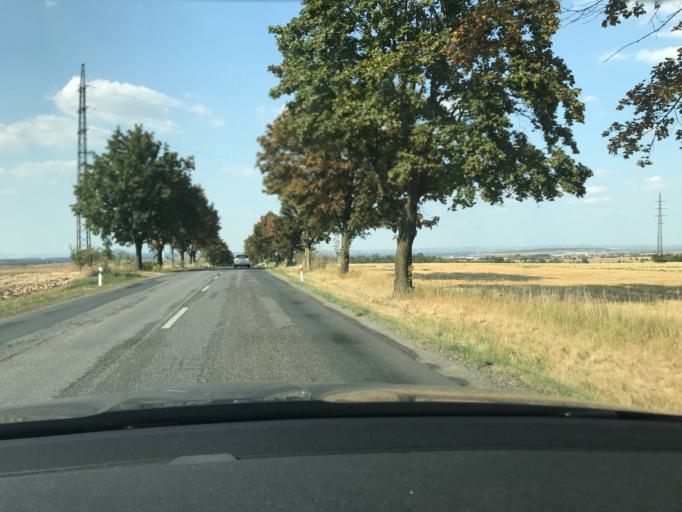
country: CZ
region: Central Bohemia
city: Kralupy nad Vltavou
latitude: 50.2118
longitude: 14.3163
